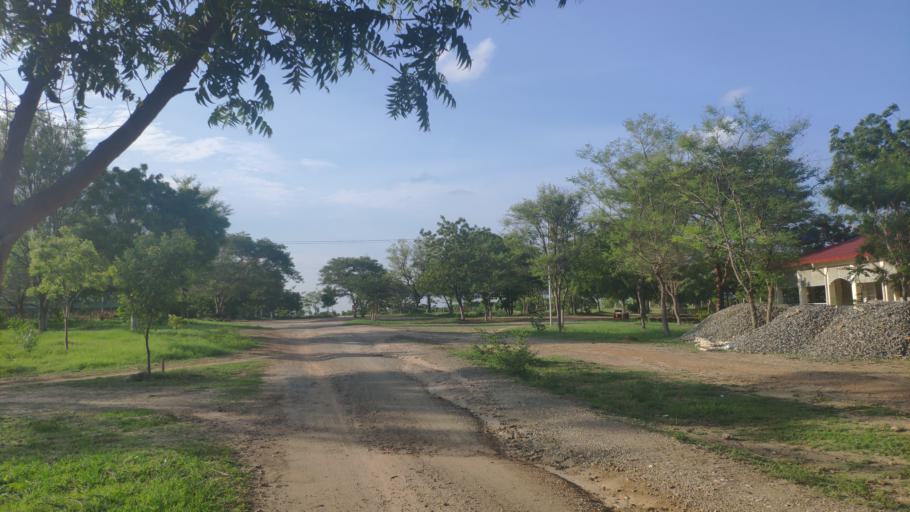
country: MM
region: Mandalay
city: Meiktila
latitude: 20.9127
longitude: 95.8606
